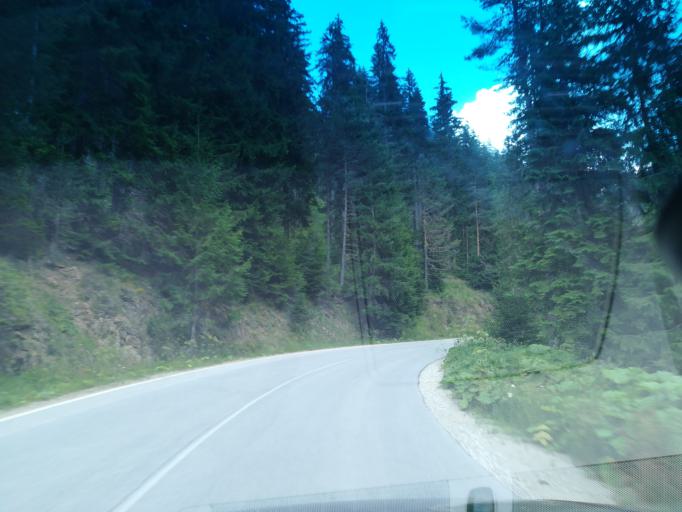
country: BG
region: Smolyan
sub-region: Obshtina Chepelare
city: Chepelare
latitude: 41.6626
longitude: 24.6573
